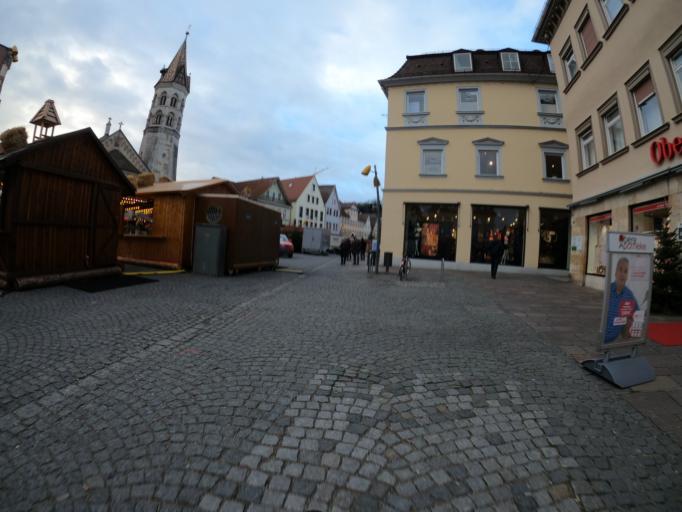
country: DE
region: Baden-Wuerttemberg
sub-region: Regierungsbezirk Stuttgart
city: Schwabisch Gmund
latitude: 48.7999
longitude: 9.7980
